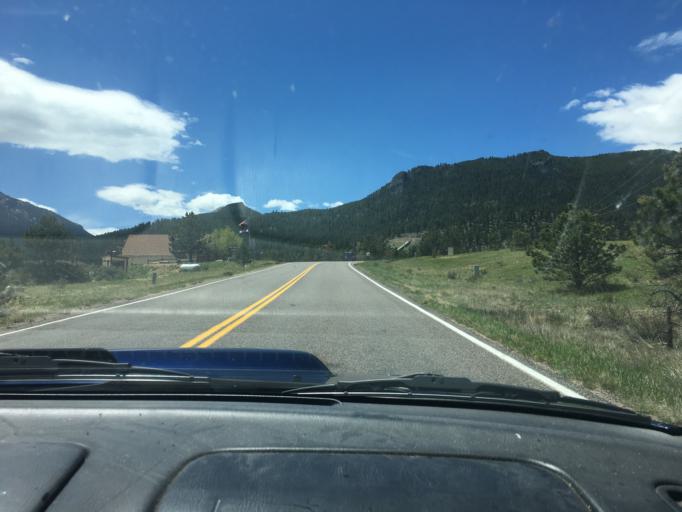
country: US
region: Colorado
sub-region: Larimer County
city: Estes Park
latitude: 40.3482
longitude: -105.5319
